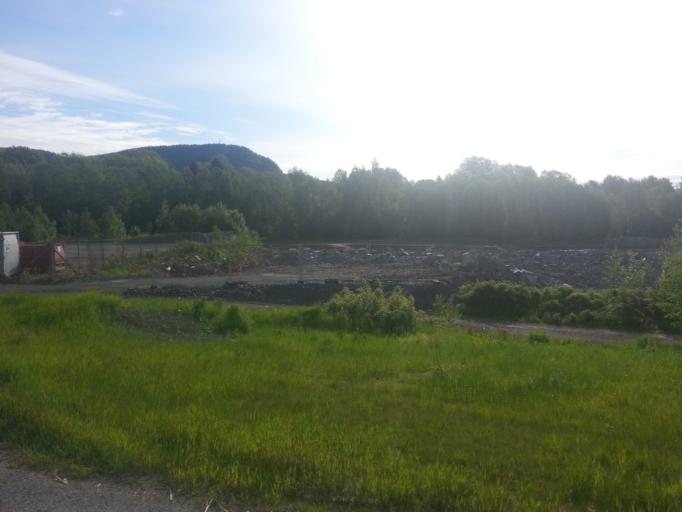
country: NO
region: Akershus
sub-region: Asker
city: Billingstad
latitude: 59.9097
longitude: 10.4792
